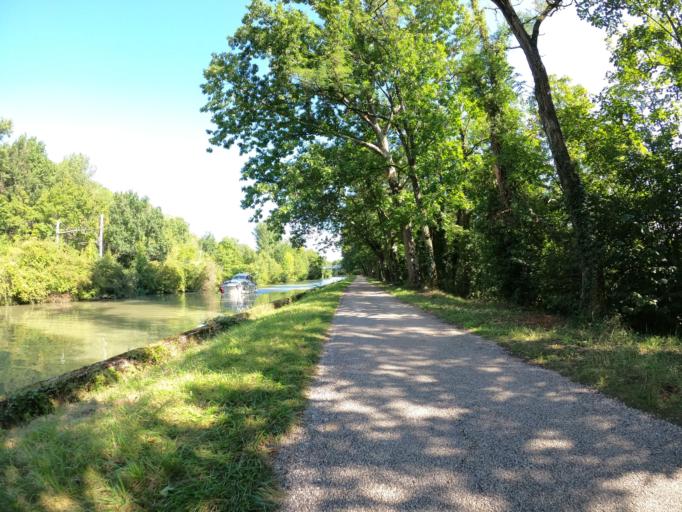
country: FR
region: Midi-Pyrenees
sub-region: Departement du Tarn-et-Garonne
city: Saint-Nicolas-de-la-Grave
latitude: 44.0936
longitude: 1.0272
